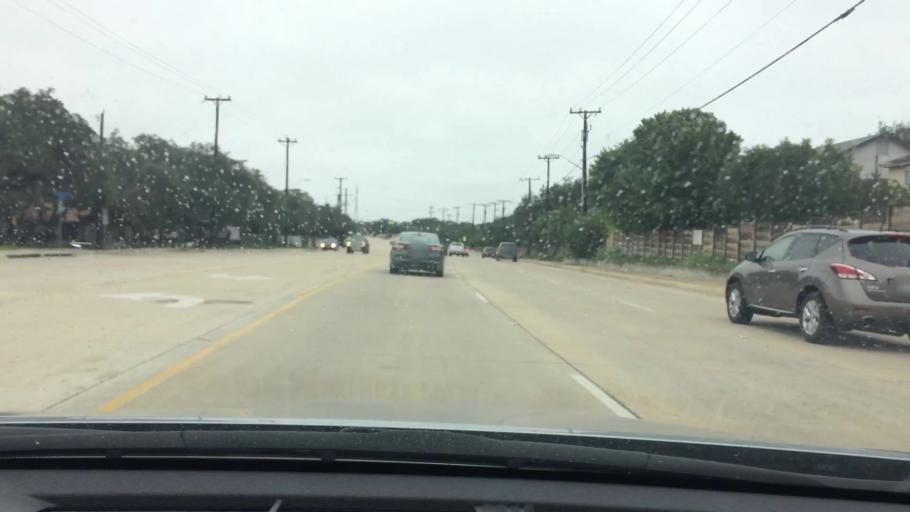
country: US
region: Texas
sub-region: Bexar County
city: Hollywood Park
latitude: 29.6424
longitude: -98.4248
